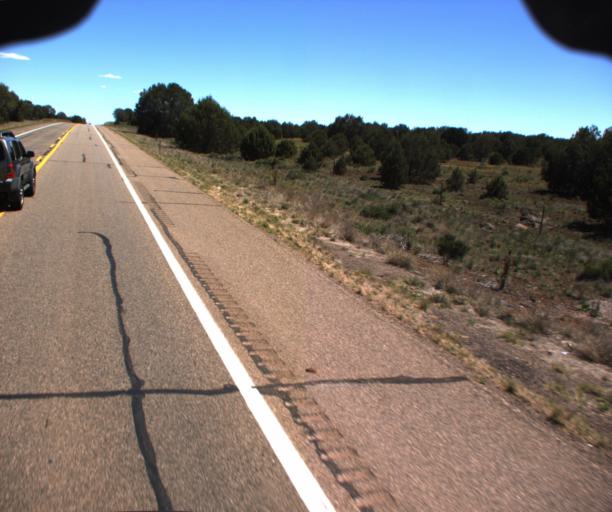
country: US
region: Arizona
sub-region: Yavapai County
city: Paulden
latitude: 35.1398
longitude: -112.4431
